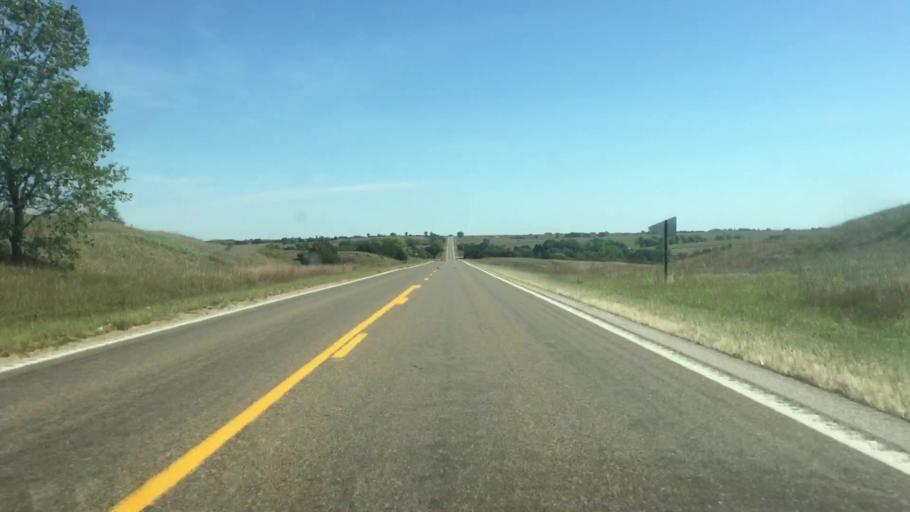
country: US
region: Nebraska
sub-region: Thayer County
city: Hebron
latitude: 40.1472
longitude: -97.5317
